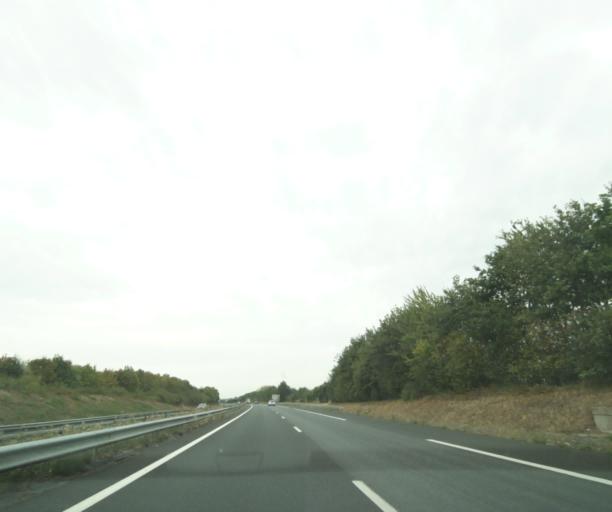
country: FR
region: Pays de la Loire
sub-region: Departement de la Vendee
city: Chauche
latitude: 46.8656
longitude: -1.2842
